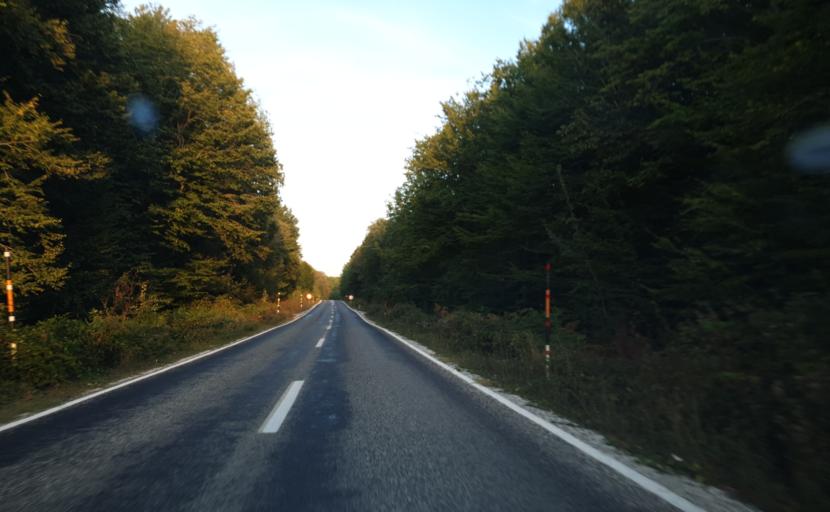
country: TR
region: Kirklareli
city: Igneada
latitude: 41.8757
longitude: 27.8231
